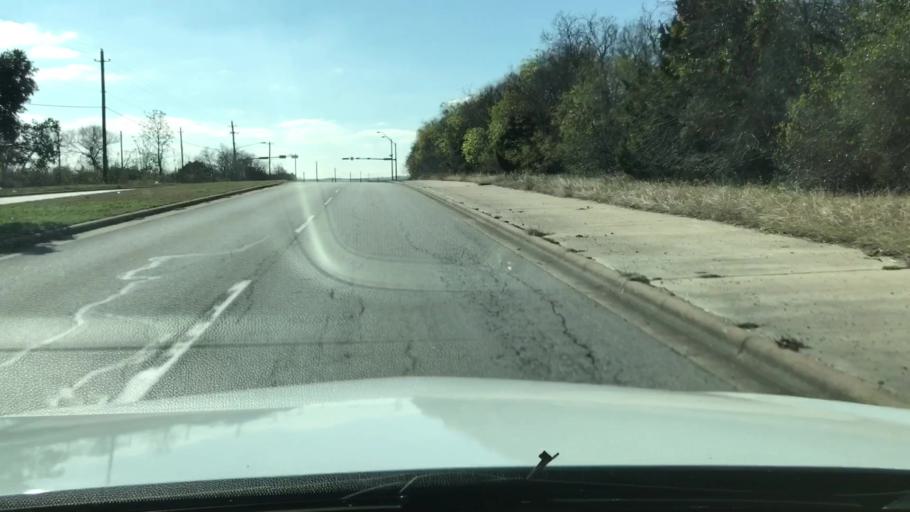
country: US
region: Texas
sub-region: Travis County
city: Onion Creek
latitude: 30.1741
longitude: -97.7221
